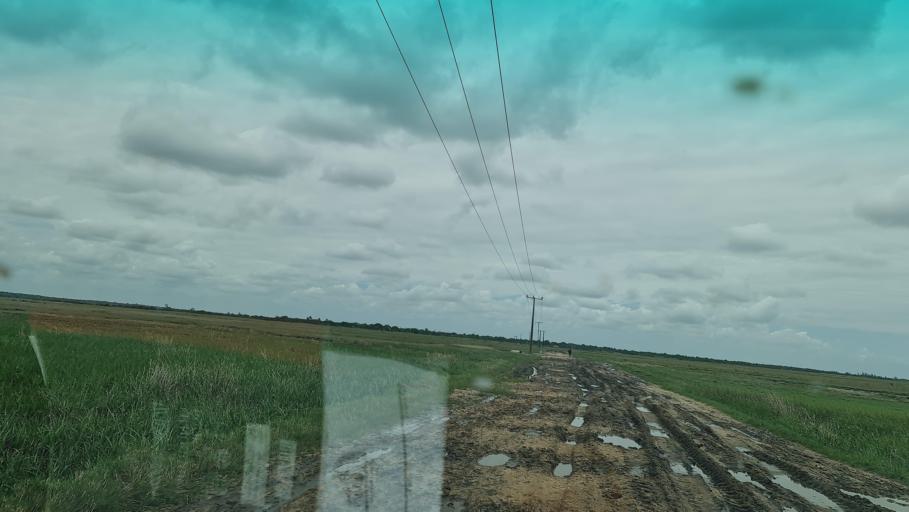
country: MZ
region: Maputo City
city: Maputo
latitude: -25.7138
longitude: 32.7025
